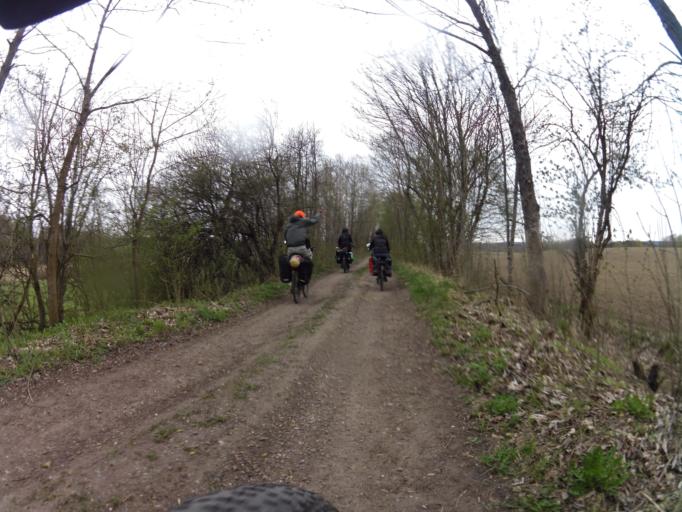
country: PL
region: West Pomeranian Voivodeship
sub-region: Powiat koszalinski
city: Bobolice
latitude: 54.0035
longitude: 16.6700
